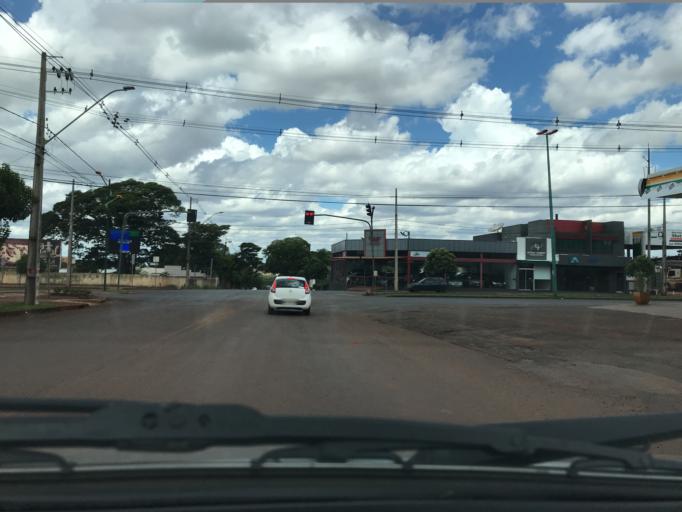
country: BR
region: Parana
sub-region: Palotina
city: Palotina
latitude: -24.2896
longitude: -53.8384
